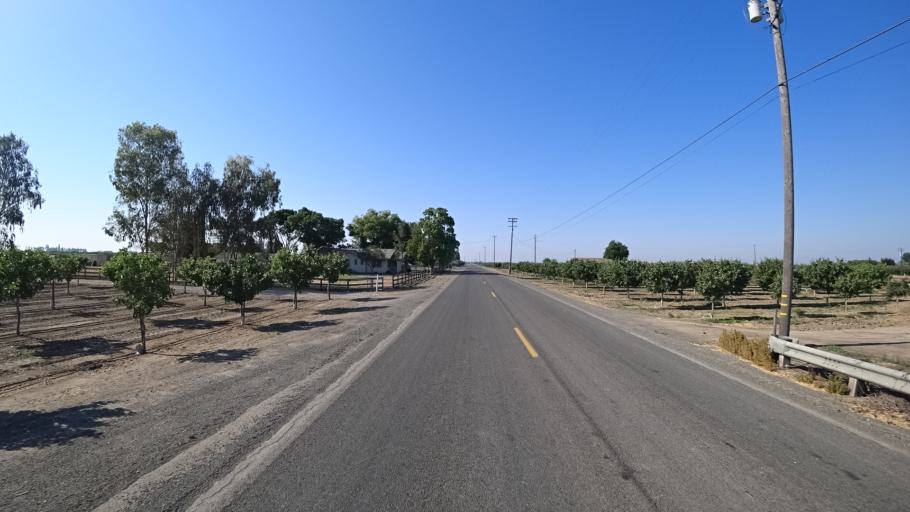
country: US
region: California
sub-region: Kings County
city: Lucerne
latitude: 36.3898
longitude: -119.6910
